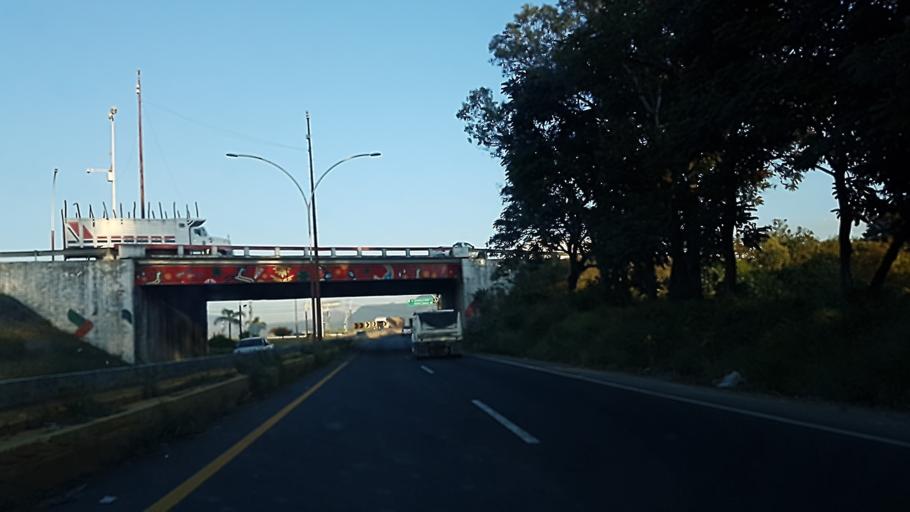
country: MX
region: Nayarit
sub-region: Tepic
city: La Corregidora
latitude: 21.4688
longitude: -104.8466
